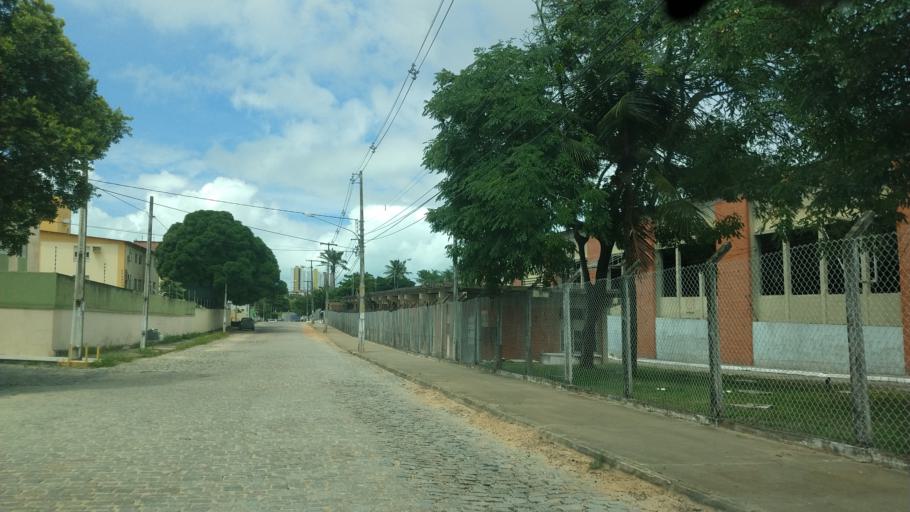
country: BR
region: Rio Grande do Norte
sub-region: Natal
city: Natal
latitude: -5.8593
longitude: -35.2127
